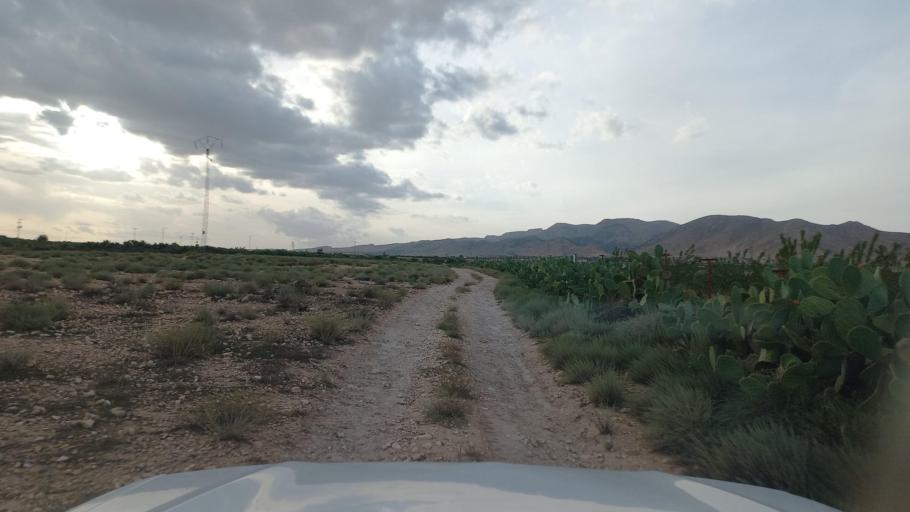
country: TN
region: Al Qasrayn
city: Sbiba
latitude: 35.4411
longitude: 9.0908
